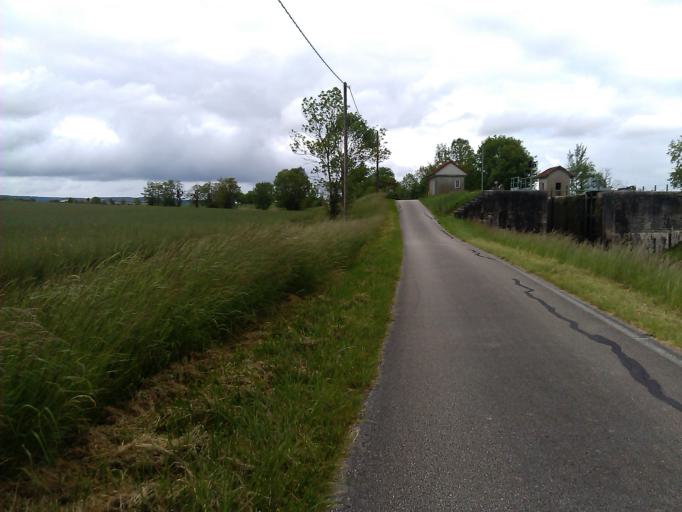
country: FR
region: Bourgogne
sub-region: Departement de Saone-et-Loire
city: Rully
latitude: 46.8848
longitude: 4.7650
